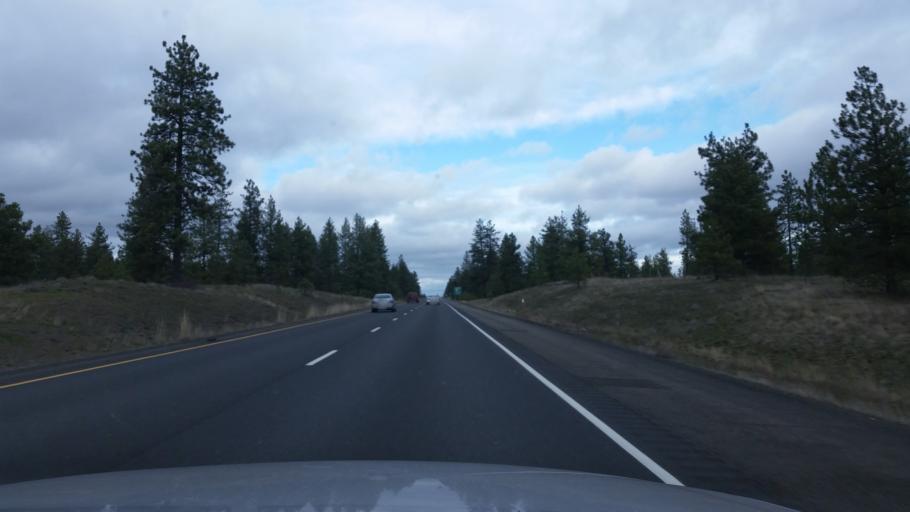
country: US
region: Washington
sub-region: Spokane County
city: Medical Lake
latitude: 47.4197
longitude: -117.8104
